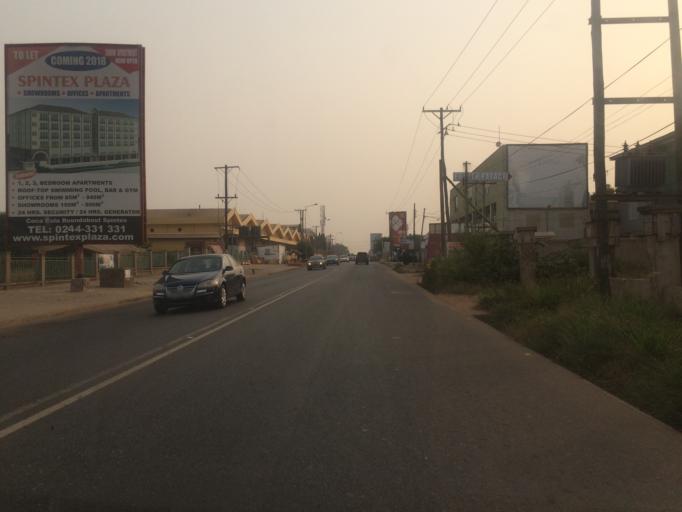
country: GH
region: Greater Accra
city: Medina Estates
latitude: 5.6414
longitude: -0.1170
